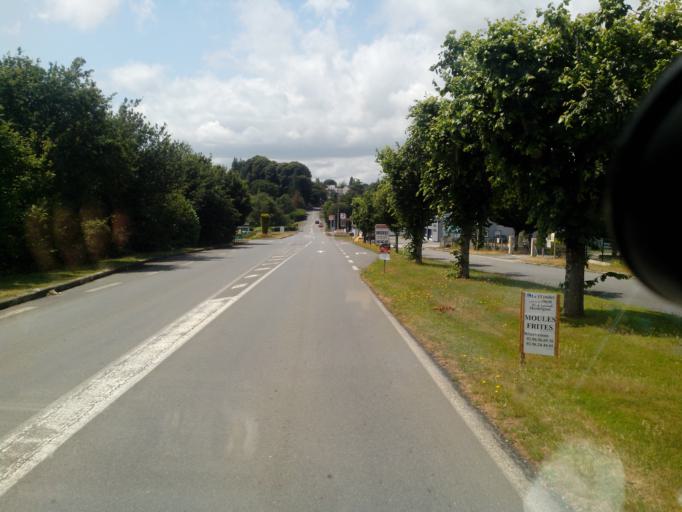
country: FR
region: Brittany
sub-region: Departement des Cotes-d'Armor
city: Merdrignac
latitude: 48.1907
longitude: -2.4015
